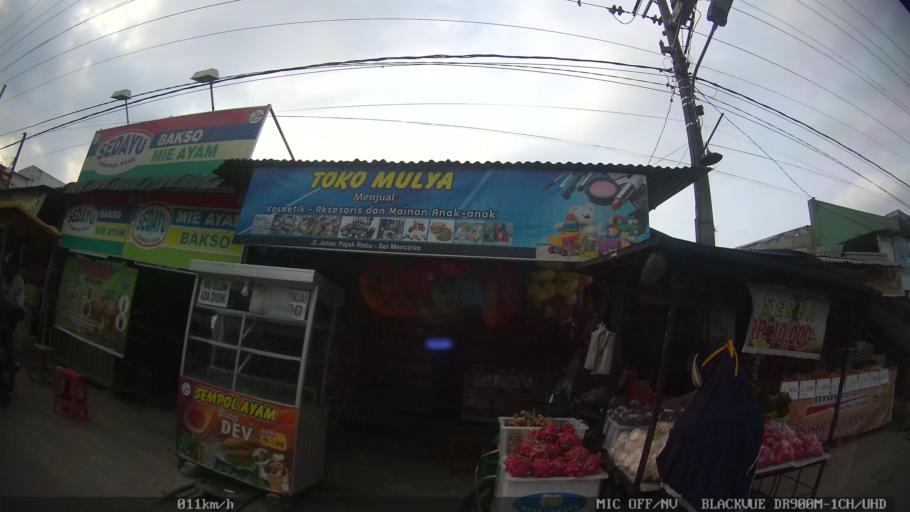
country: ID
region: North Sumatra
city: Sunggal
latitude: 3.5576
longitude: 98.5519
